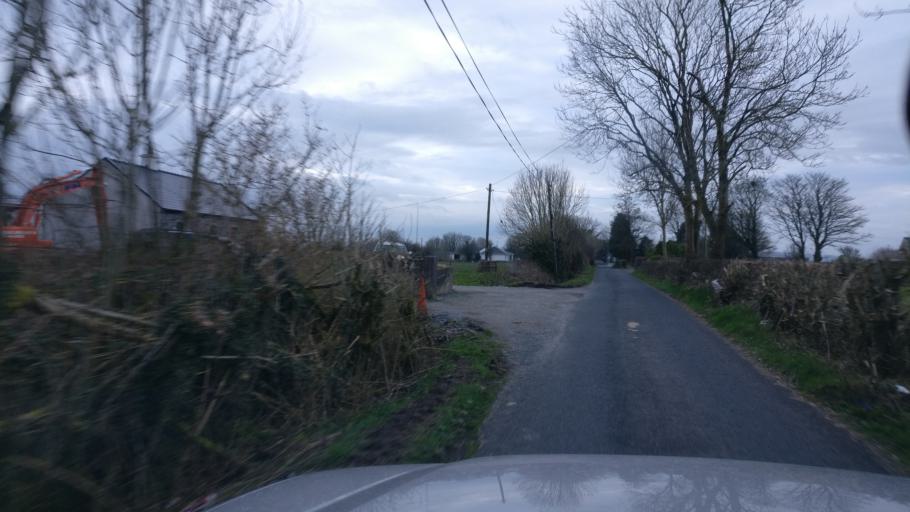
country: IE
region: Connaught
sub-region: County Galway
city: Loughrea
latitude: 53.2532
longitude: -8.5111
